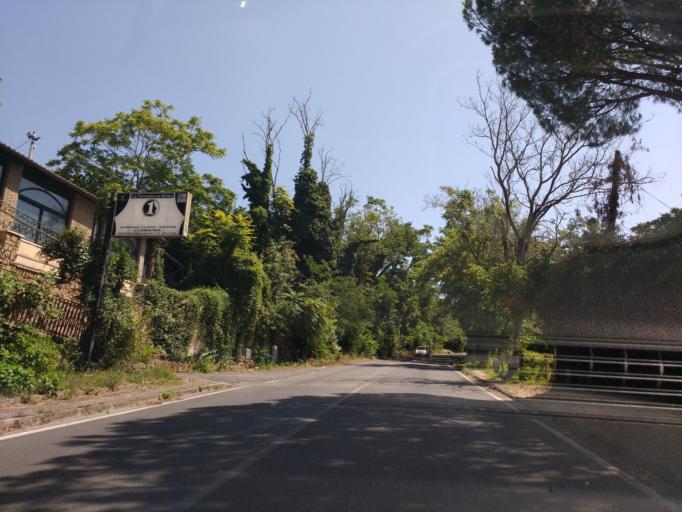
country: IT
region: Latium
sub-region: Citta metropolitana di Roma Capitale
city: Grottaferrata
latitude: 41.7978
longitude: 12.6825
